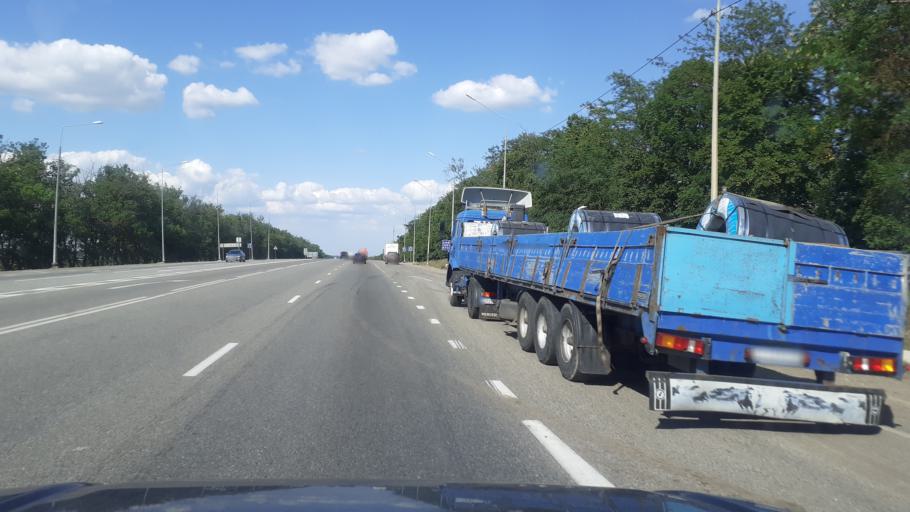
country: RU
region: Krasnodarskiy
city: Severskaya
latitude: 44.8392
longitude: 38.6944
